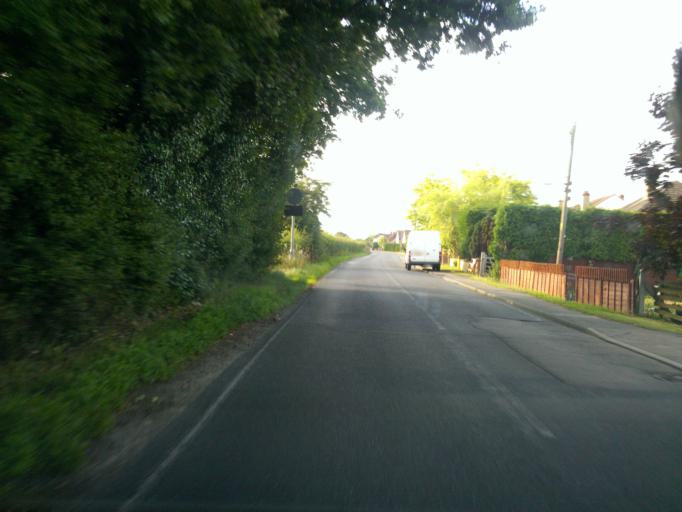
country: GB
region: England
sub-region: Essex
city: Great Bentley
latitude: 51.8393
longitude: 1.0707
